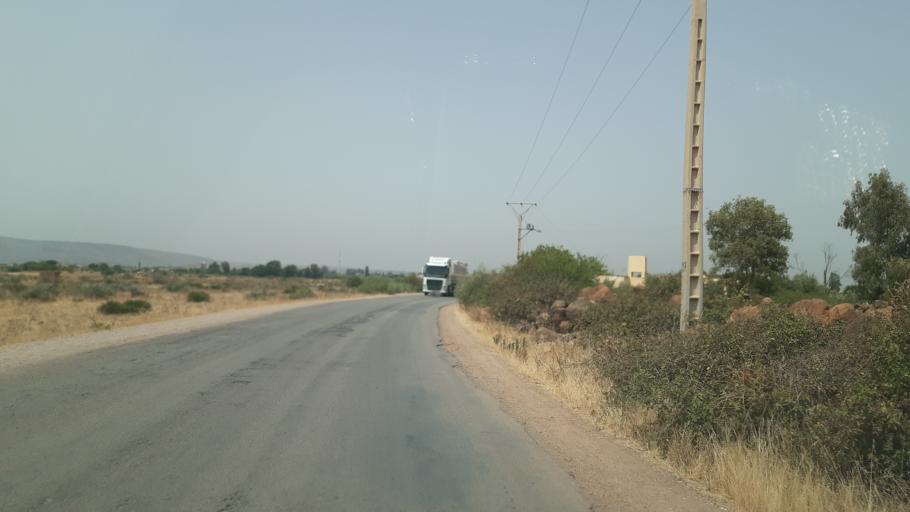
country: MA
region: Fes-Boulemane
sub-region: Fes
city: Oulad Tayeb
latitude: 33.8367
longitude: -5.1353
